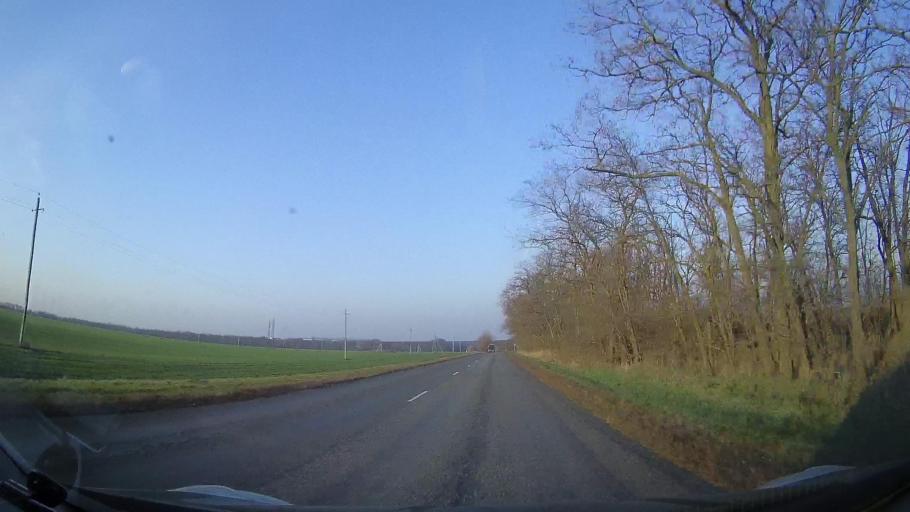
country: RU
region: Rostov
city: Ol'ginskaya
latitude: 47.1046
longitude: 39.9776
